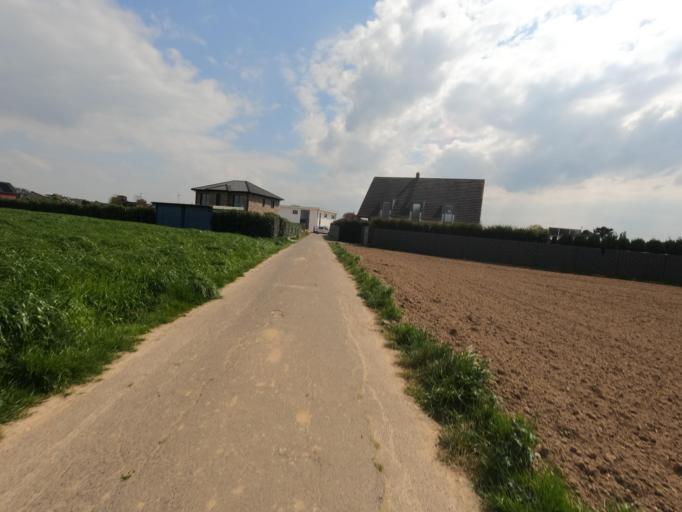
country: DE
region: North Rhine-Westphalia
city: Huckelhoven
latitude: 51.0798
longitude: 6.2201
